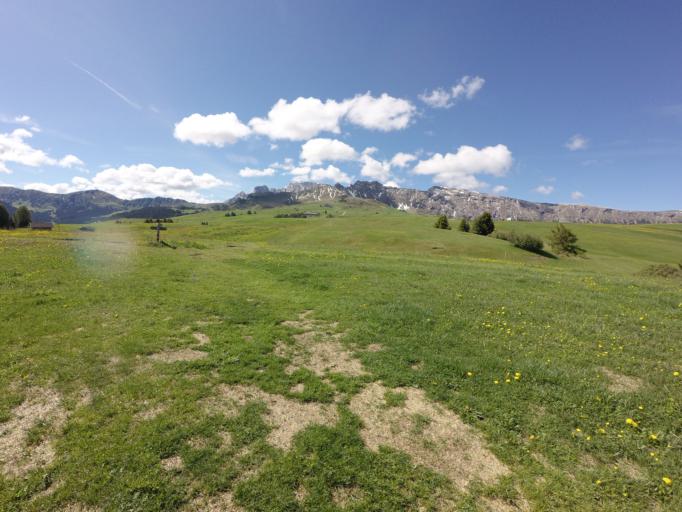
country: IT
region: Trentino-Alto Adige
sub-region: Bolzano
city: Ortisei
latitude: 46.5371
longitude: 11.6372
